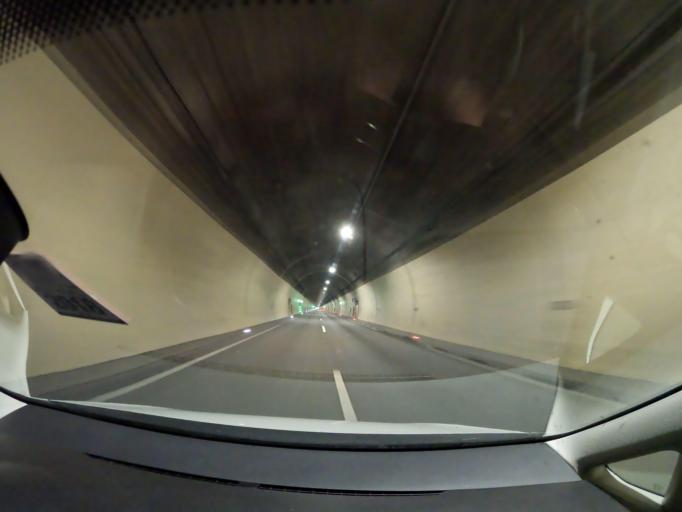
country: AT
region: Carinthia
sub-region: Politischer Bezirk Wolfsberg
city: Bad Sankt Leonhard im Lavanttal
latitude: 46.9062
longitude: 14.8220
